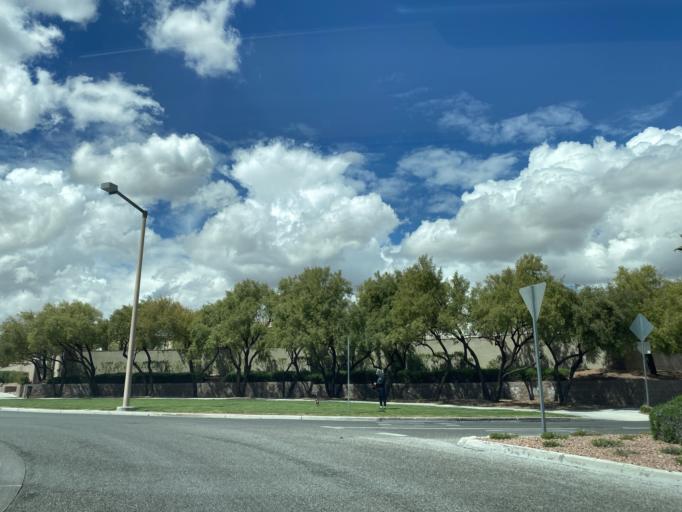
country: US
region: Nevada
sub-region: Clark County
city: Summerlin South
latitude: 36.1409
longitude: -115.3312
